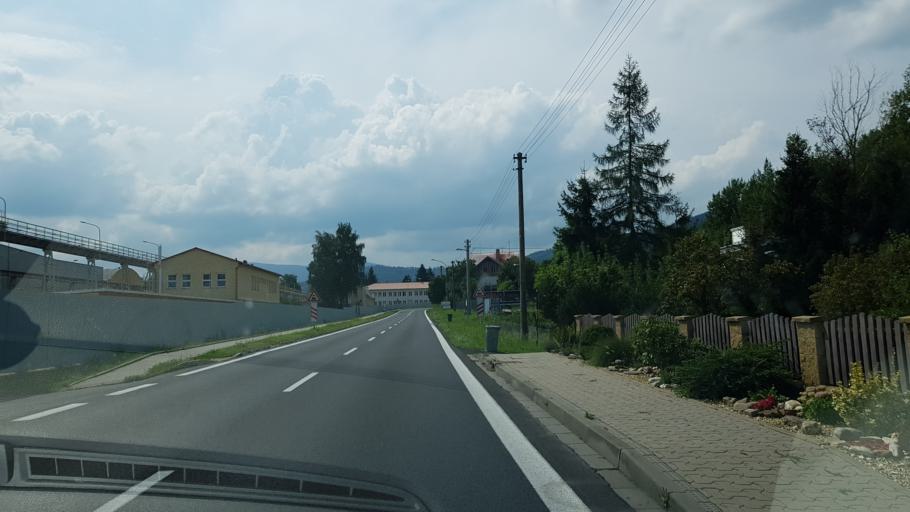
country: CZ
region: Olomoucky
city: Ceska Ves
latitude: 50.2589
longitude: 17.2317
